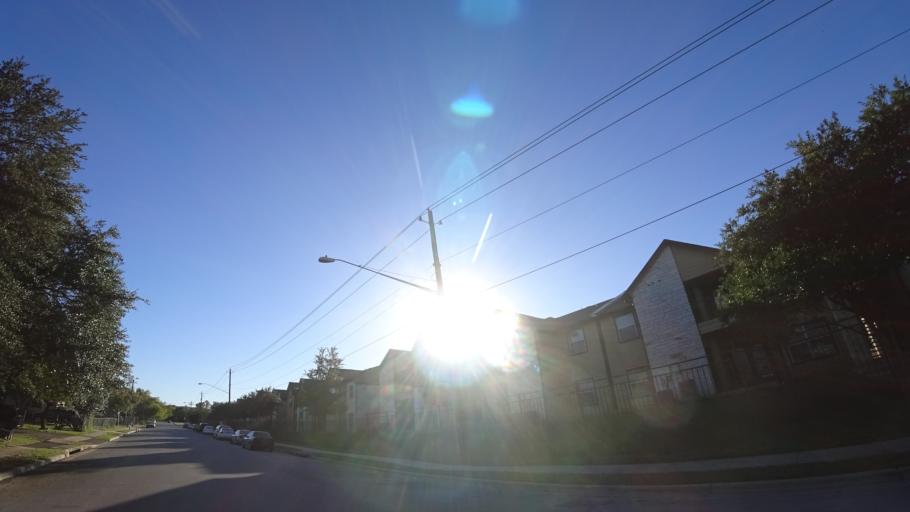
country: US
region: Texas
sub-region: Travis County
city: Austin
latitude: 30.2285
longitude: -97.7048
